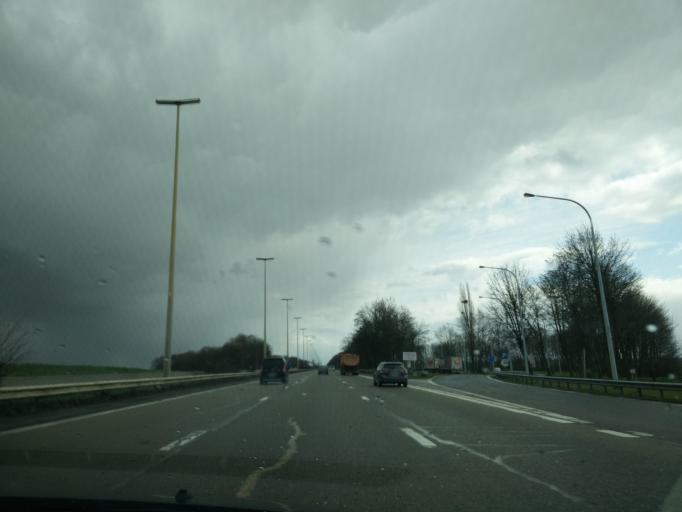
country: BE
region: Wallonia
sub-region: Province de Liege
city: Fexhe-le-Haut-Clocher
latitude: 50.6888
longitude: 5.4104
